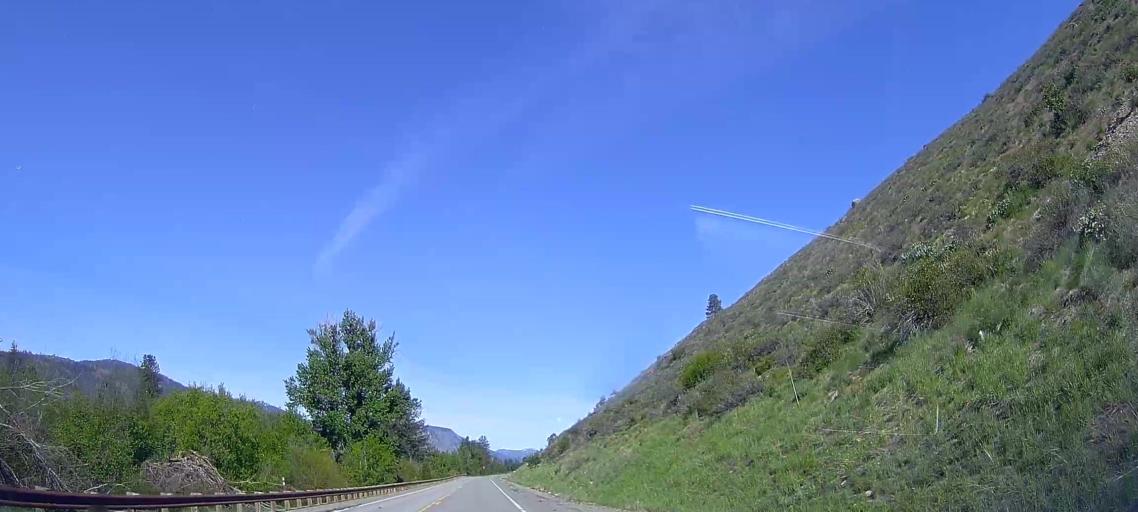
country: US
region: Washington
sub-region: Chelan County
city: Granite Falls
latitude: 48.4966
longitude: -120.2412
